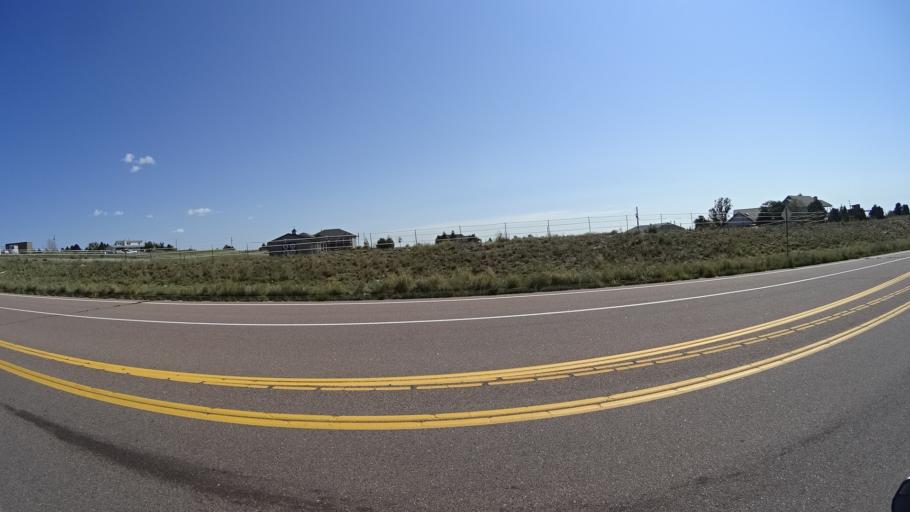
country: US
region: Colorado
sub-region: El Paso County
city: Cimarron Hills
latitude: 38.9331
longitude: -104.7015
